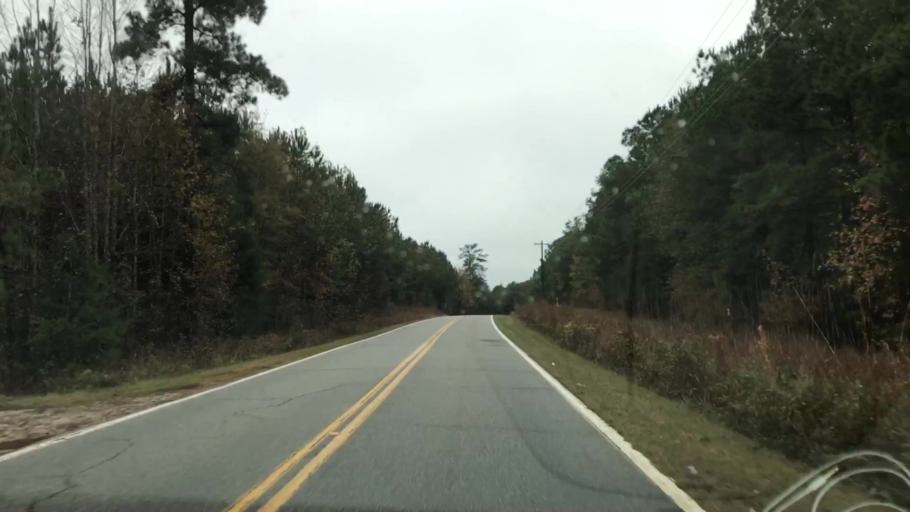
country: US
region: South Carolina
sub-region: Greenwood County
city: Ninety Six
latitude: 34.2889
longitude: -81.9765
